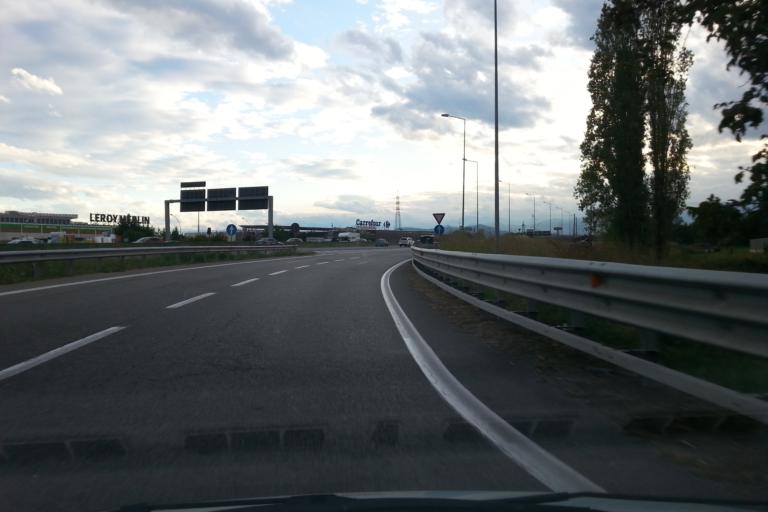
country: IT
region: Piedmont
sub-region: Provincia di Torino
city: Savonera
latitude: 45.1042
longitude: 7.5965
